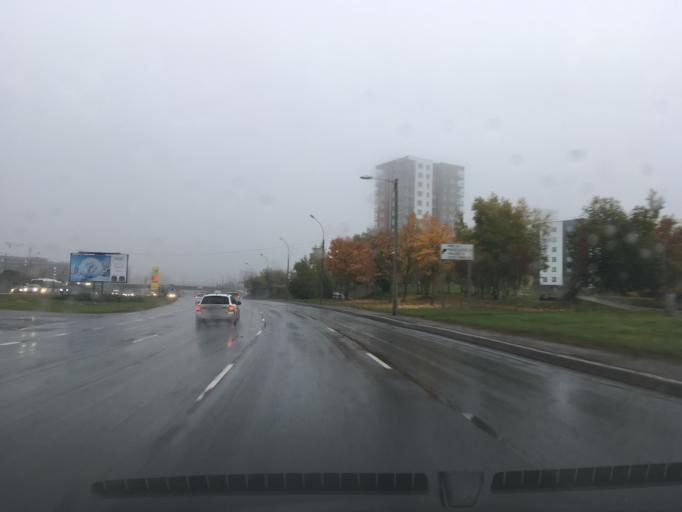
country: EE
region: Harju
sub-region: Tallinna linn
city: Tallinn
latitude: 59.4349
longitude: 24.8048
